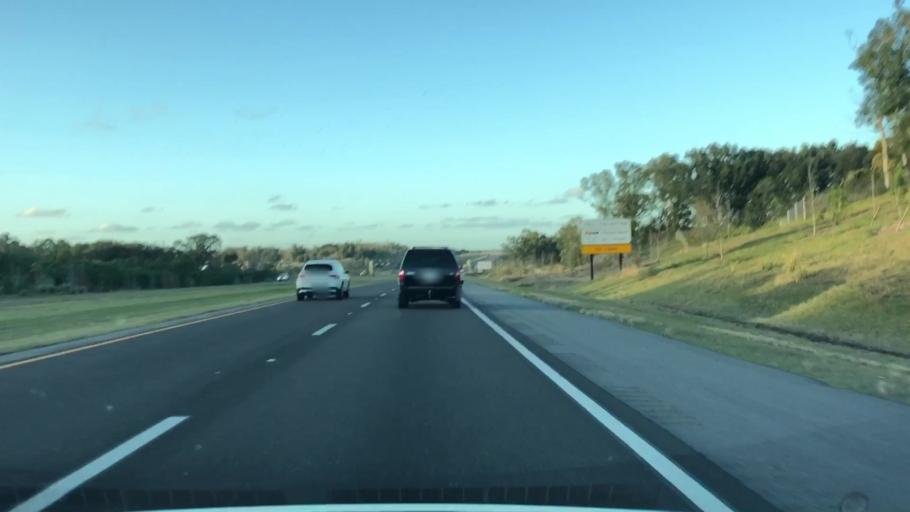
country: US
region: Florida
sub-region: Orange County
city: Zellwood
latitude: 28.7169
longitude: -81.5619
